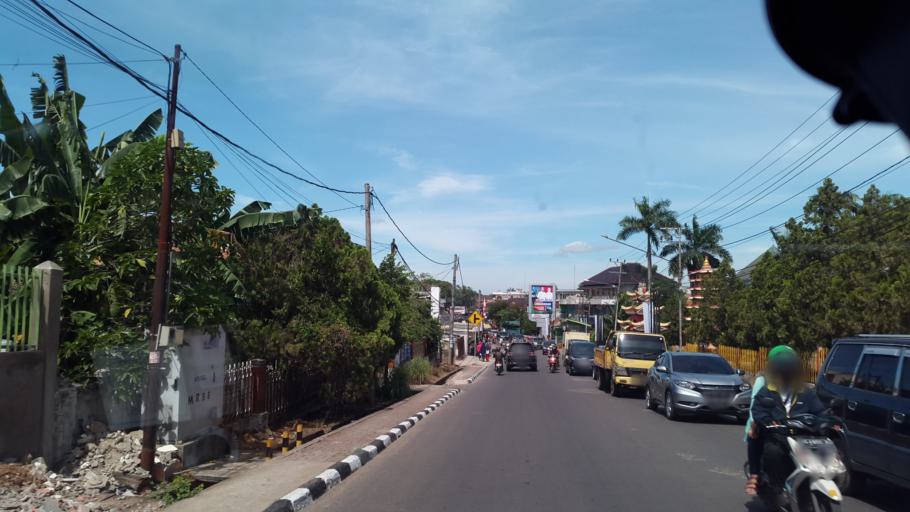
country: ID
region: South Sumatra
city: Plaju
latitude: -2.9893
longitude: 104.7348
